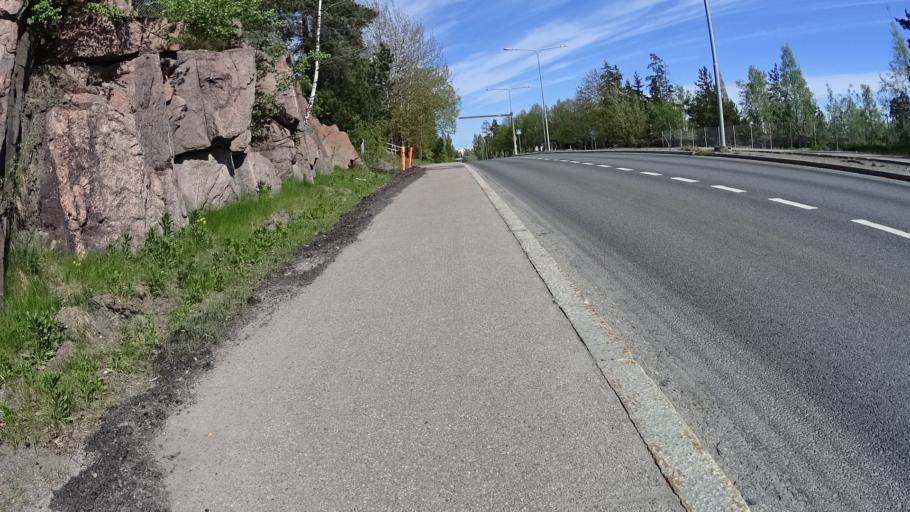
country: FI
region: Uusimaa
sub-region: Helsinki
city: Vantaa
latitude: 60.2974
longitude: 24.9429
